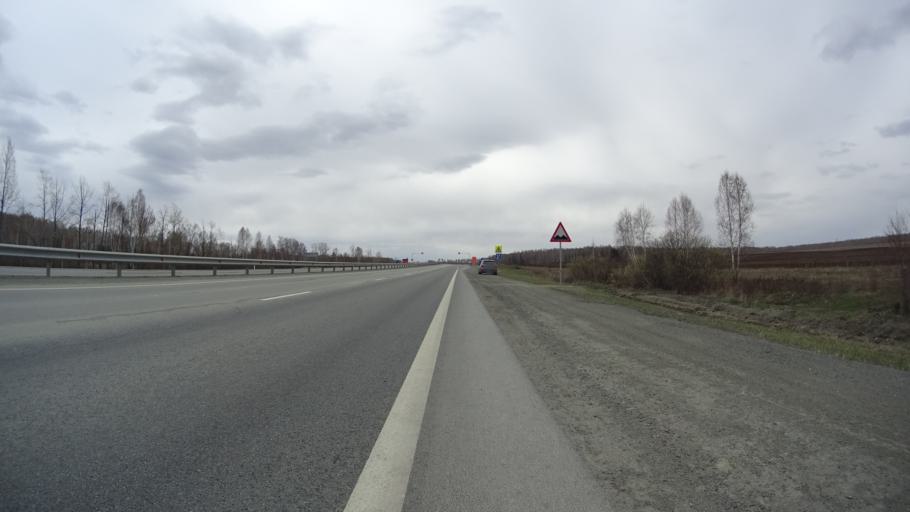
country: RU
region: Chelyabinsk
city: Yemanzhelinka
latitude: 54.8259
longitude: 61.3101
